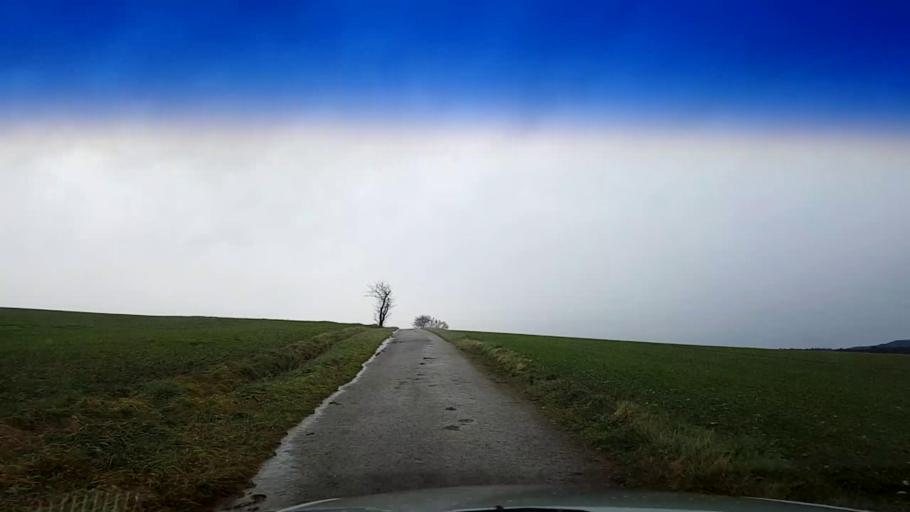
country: DE
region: Bavaria
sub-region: Upper Franconia
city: Memmelsdorf
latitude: 49.9646
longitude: 10.9806
